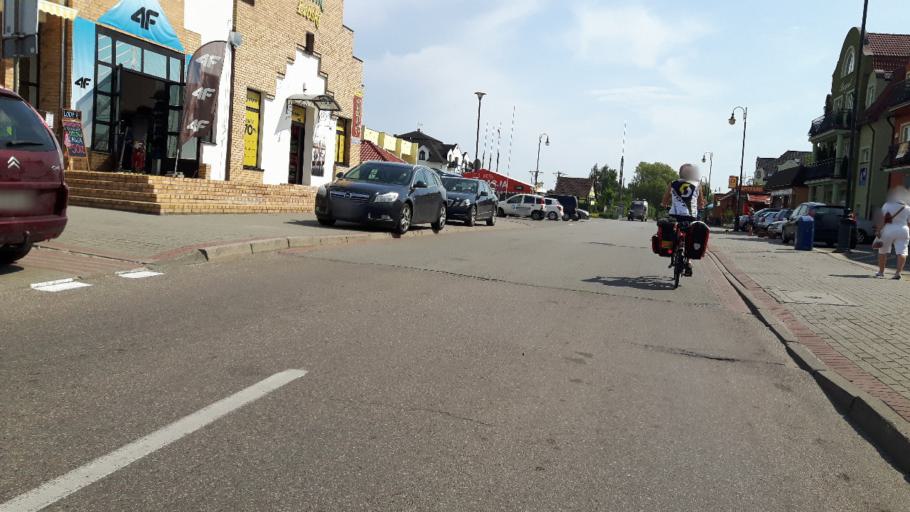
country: PL
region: Pomeranian Voivodeship
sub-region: Powiat leborski
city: Leba
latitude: 54.7589
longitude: 17.5569
